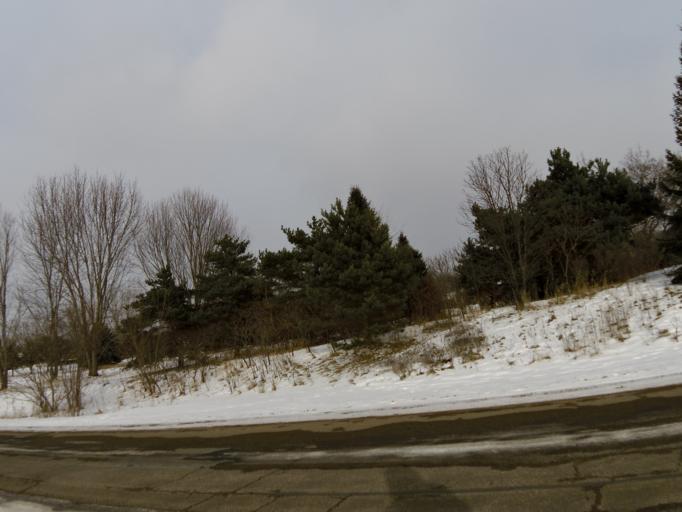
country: US
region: Minnesota
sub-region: Washington County
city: Lake Elmo
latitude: 44.9730
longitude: -92.8490
